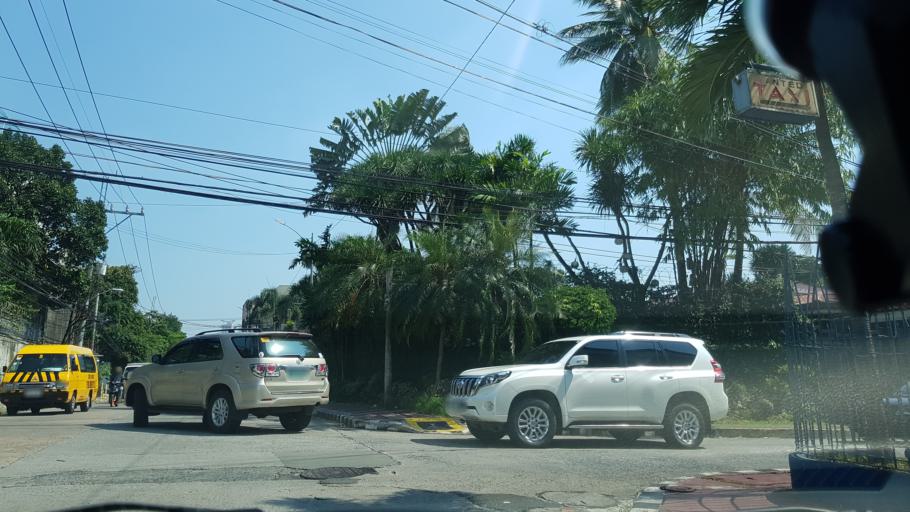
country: PH
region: Calabarzon
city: Del Monte
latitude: 14.6208
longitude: 121.0246
